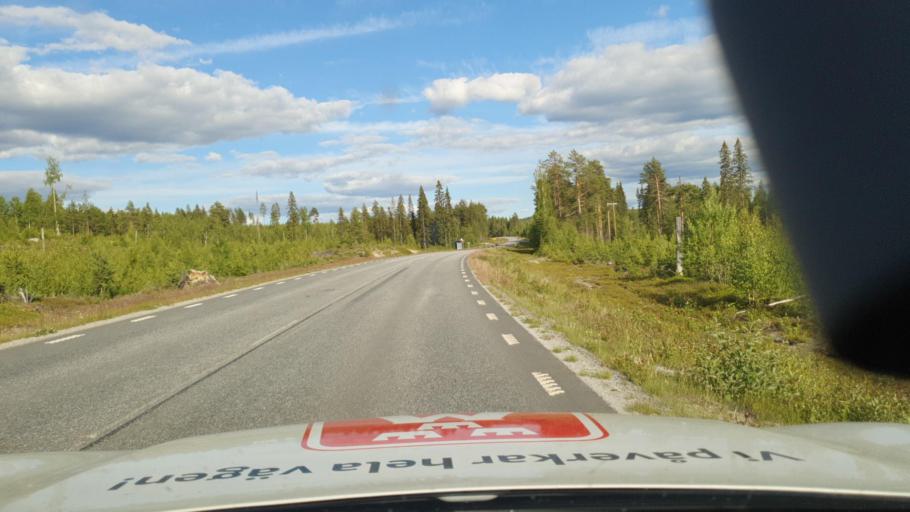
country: SE
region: Vaesterbotten
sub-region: Lycksele Kommun
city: Lycksele
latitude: 64.5177
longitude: 18.8475
